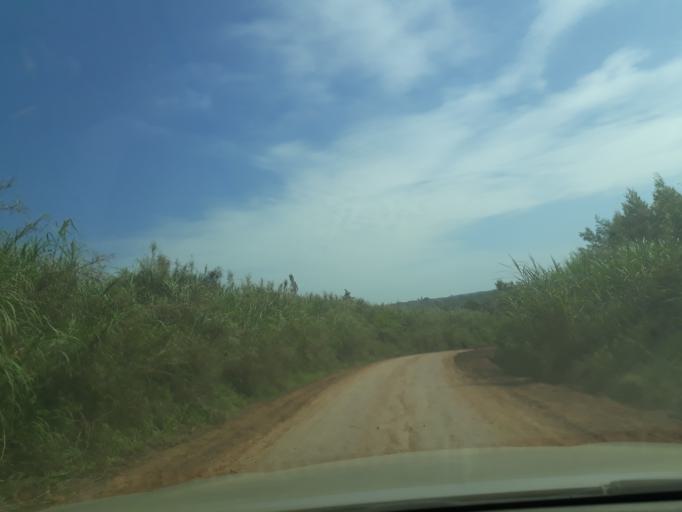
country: CD
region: Eastern Province
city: Bunia
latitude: 1.9328
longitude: 30.5152
